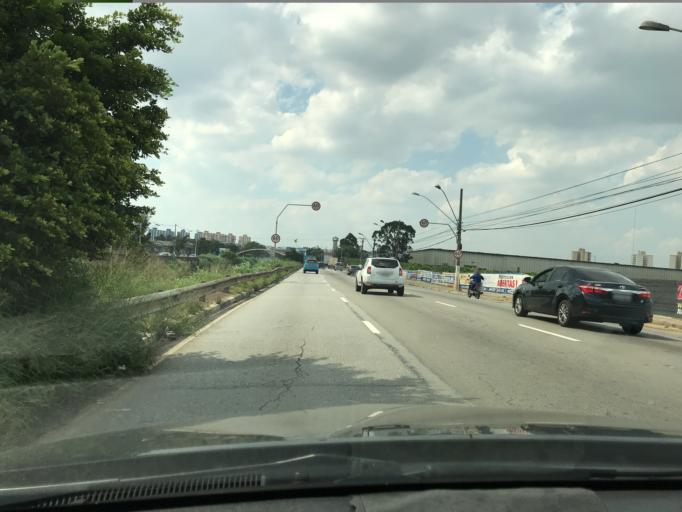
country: BR
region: Sao Paulo
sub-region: Sao Caetano Do Sul
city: Sao Caetano do Sul
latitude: -23.6171
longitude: -46.5429
